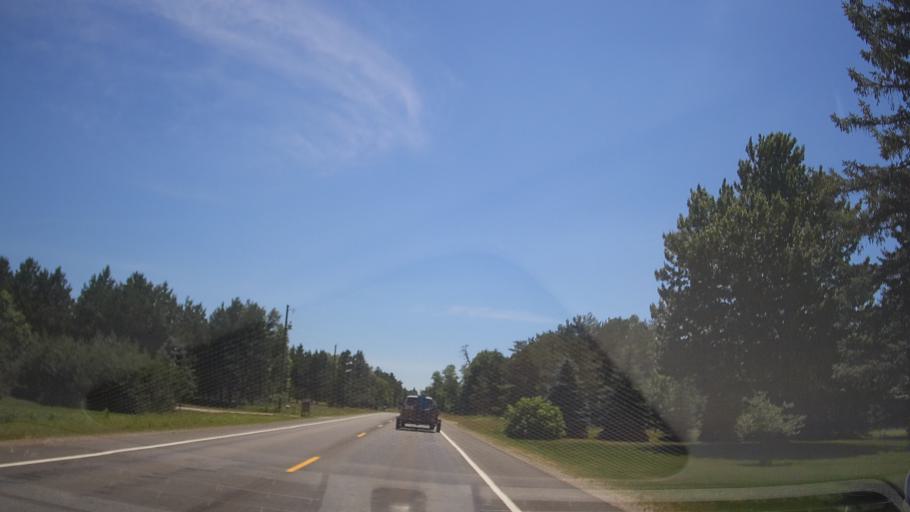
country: US
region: Michigan
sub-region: Grand Traverse County
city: Traverse City
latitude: 44.6417
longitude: -85.6964
